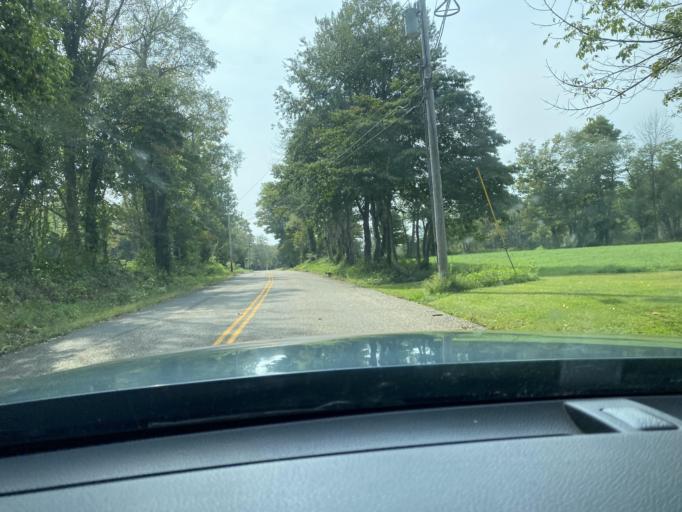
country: US
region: Connecticut
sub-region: New London County
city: Colchester
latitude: 41.6230
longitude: -72.3070
